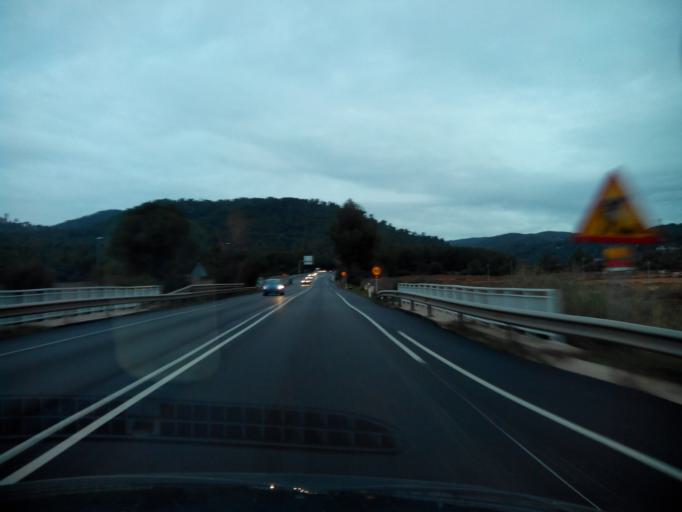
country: ES
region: Catalonia
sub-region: Provincia de Barcelona
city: Viladecavalls
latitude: 41.5644
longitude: 1.9652
